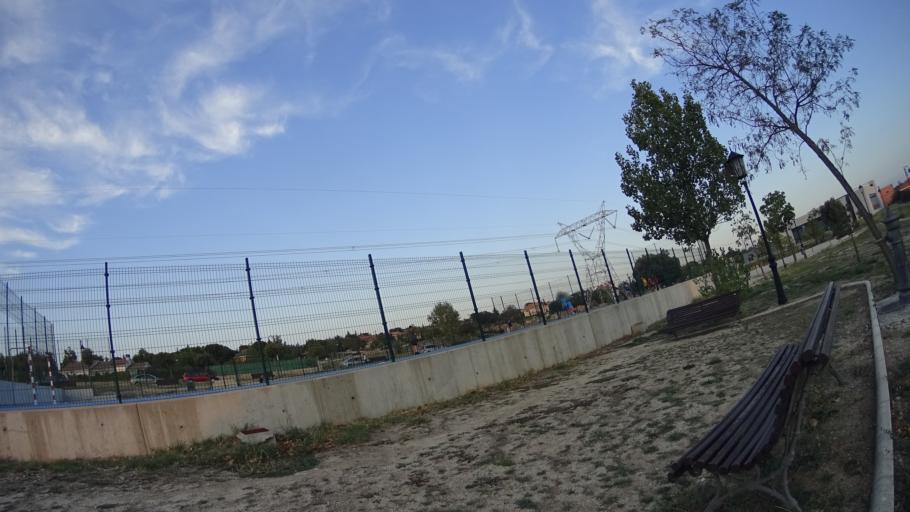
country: ES
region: Madrid
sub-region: Provincia de Madrid
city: Galapagar
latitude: 40.5851
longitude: -3.9987
